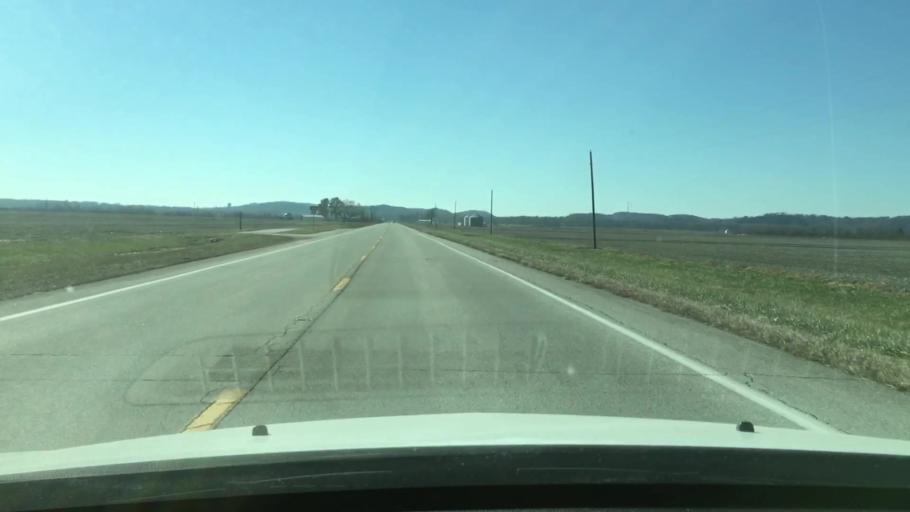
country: US
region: Missouri
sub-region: Pike County
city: Louisiana
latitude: 39.4839
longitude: -91.0149
